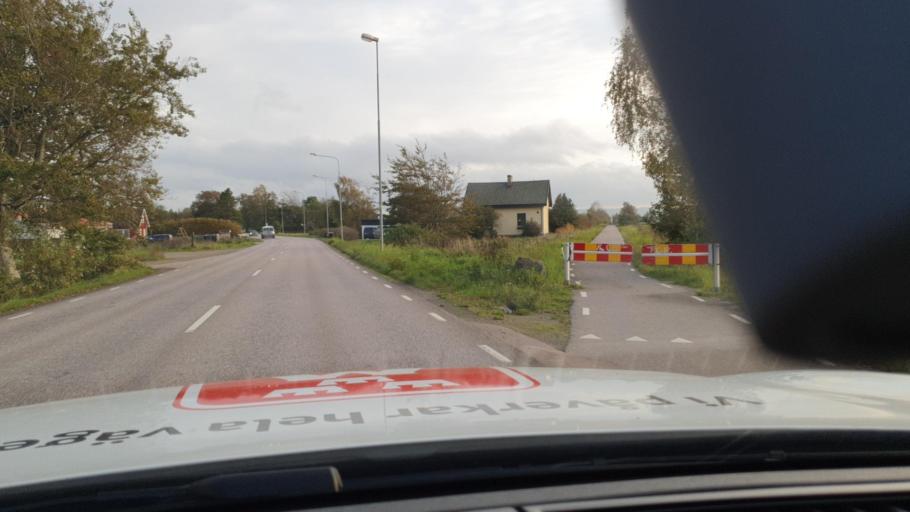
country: SE
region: Halland
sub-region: Laholms Kommun
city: Laholm
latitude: 56.4946
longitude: 13.0355
